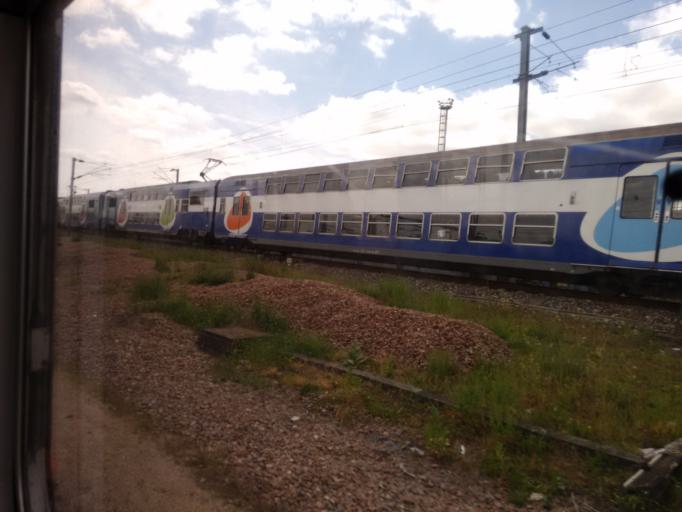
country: FR
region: Ile-de-France
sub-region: Paris
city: Saint-Ouen
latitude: 48.9036
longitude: 2.3538
